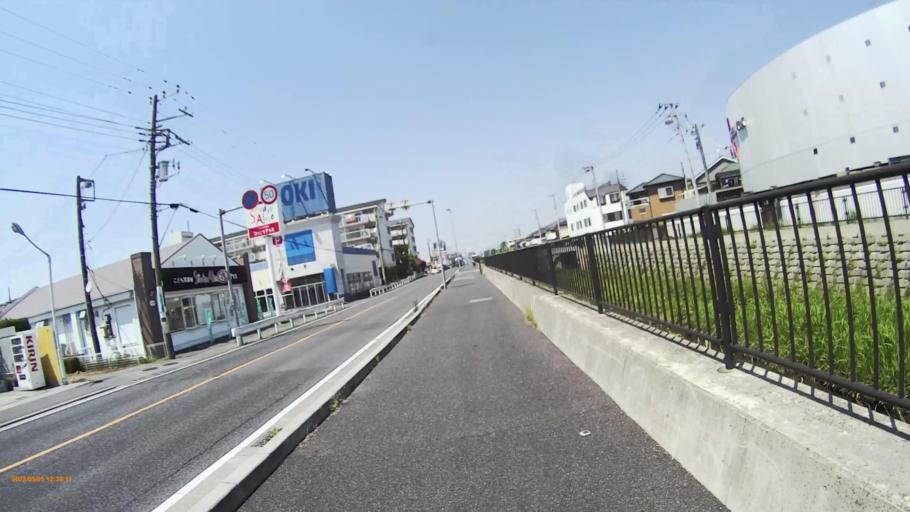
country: JP
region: Saitama
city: Kasukabe
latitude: 35.9385
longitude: 139.7772
